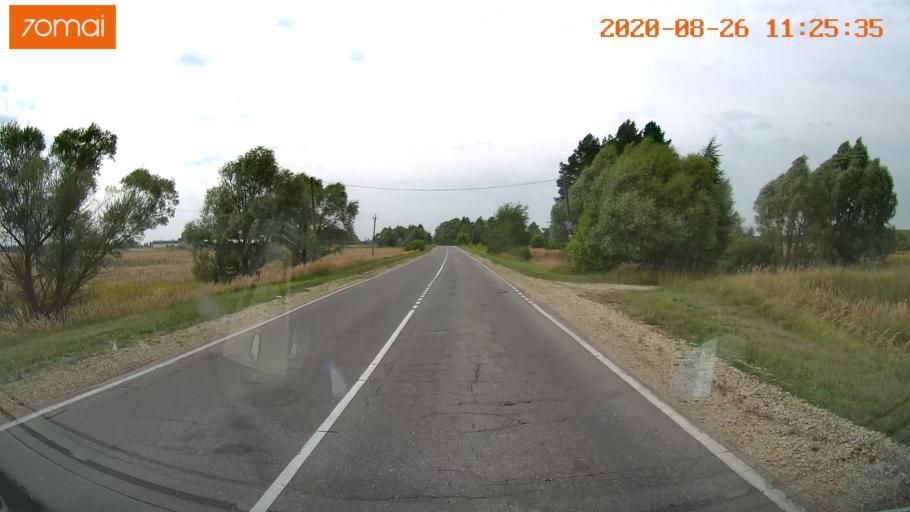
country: RU
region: Rjazan
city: Shilovo
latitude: 54.3408
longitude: 40.9616
